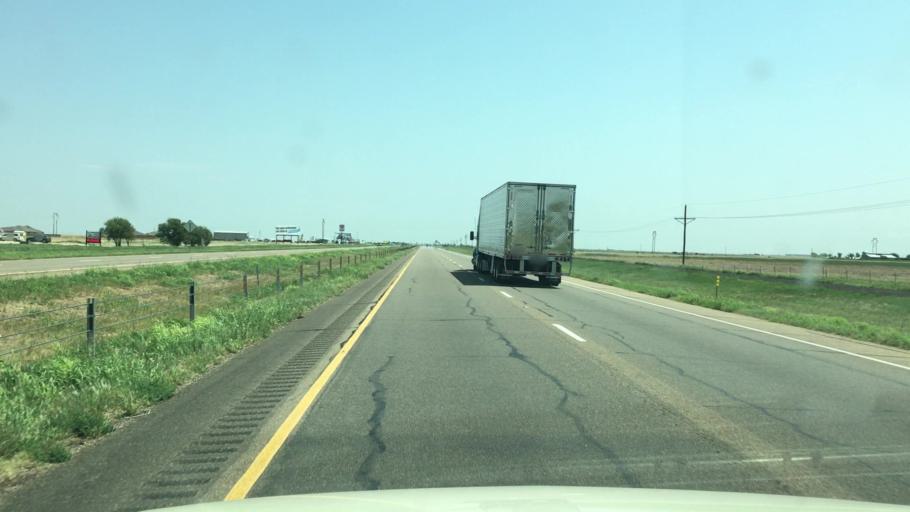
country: US
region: Texas
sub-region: Potter County
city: Bushland
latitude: 35.1908
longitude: -102.0554
